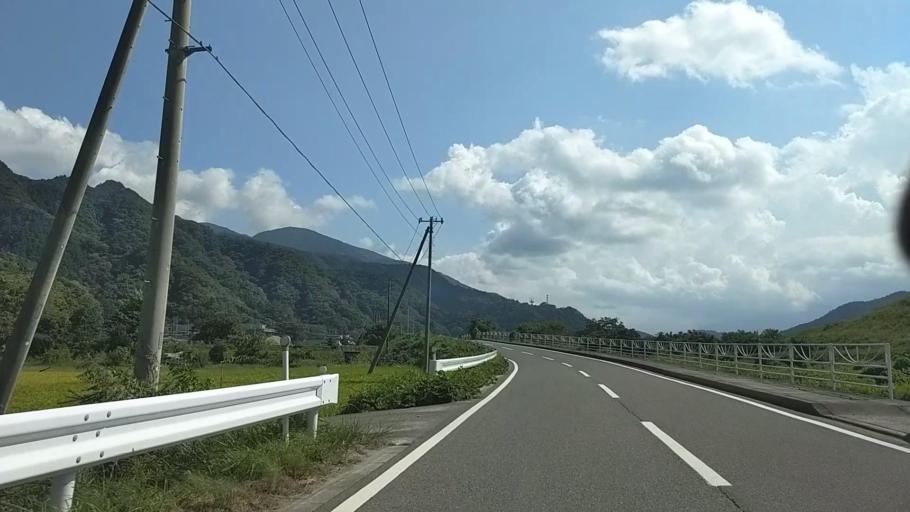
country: JP
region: Shizuoka
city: Fujinomiya
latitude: 35.3894
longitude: 138.4518
